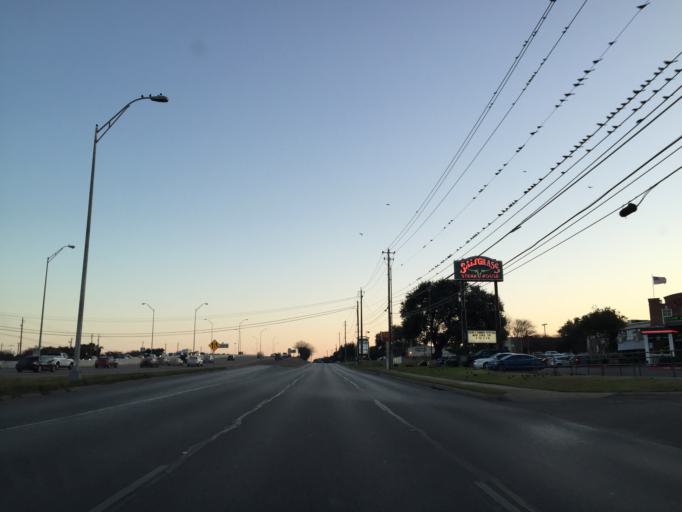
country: US
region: Texas
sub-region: Williamson County
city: Jollyville
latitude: 30.3983
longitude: -97.7465
